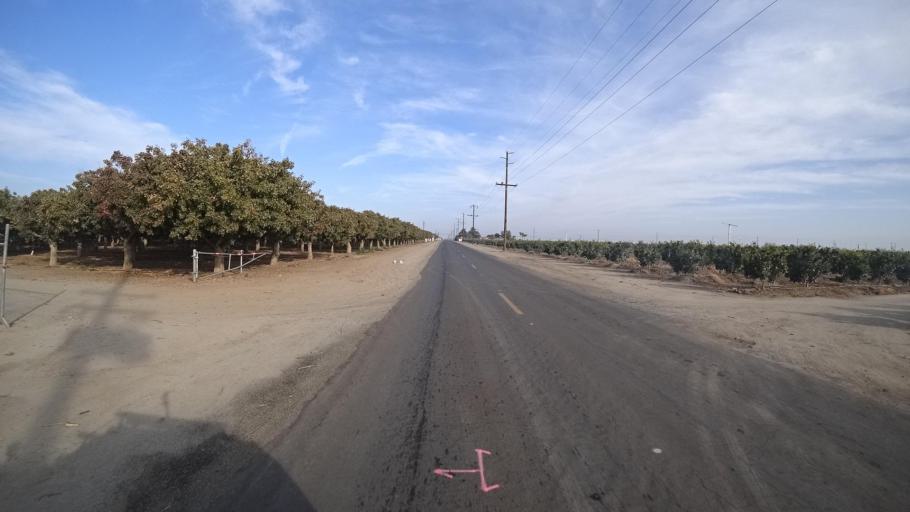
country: US
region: California
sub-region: Kern County
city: Delano
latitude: 35.7723
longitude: -119.2053
